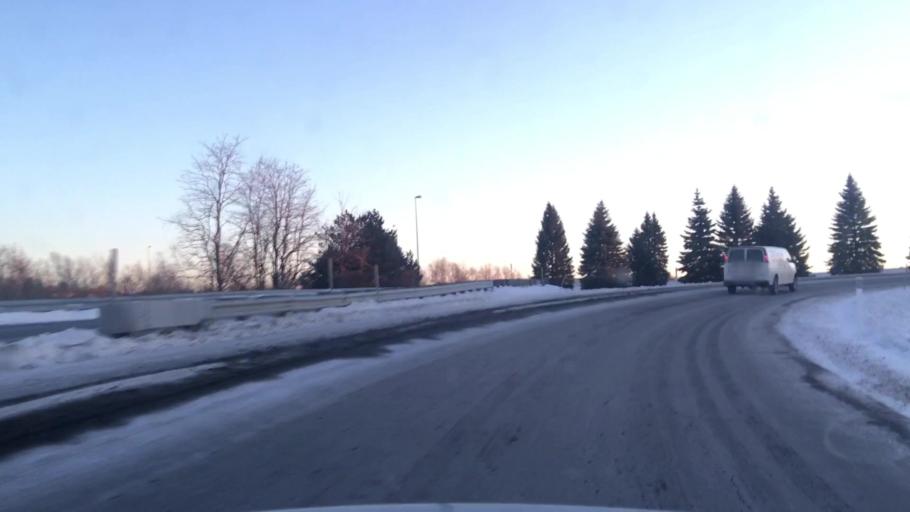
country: US
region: Maine
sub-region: Penobscot County
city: Brewer
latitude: 44.7848
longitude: -68.7699
